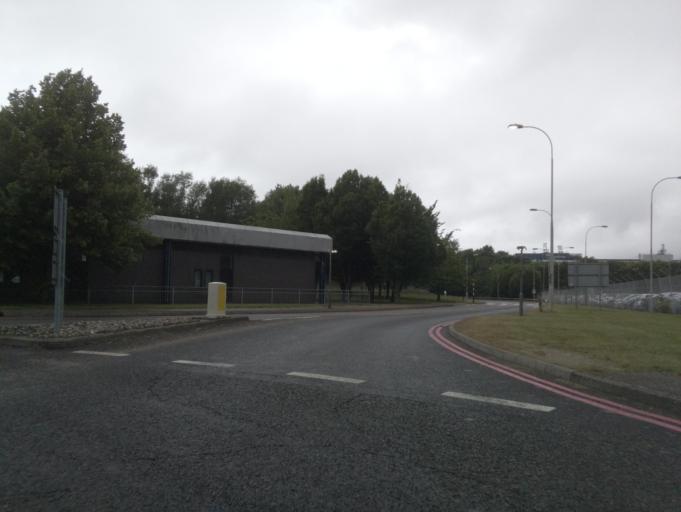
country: GB
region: England
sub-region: Surrey
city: Horley
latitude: 51.1638
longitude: -0.1753
